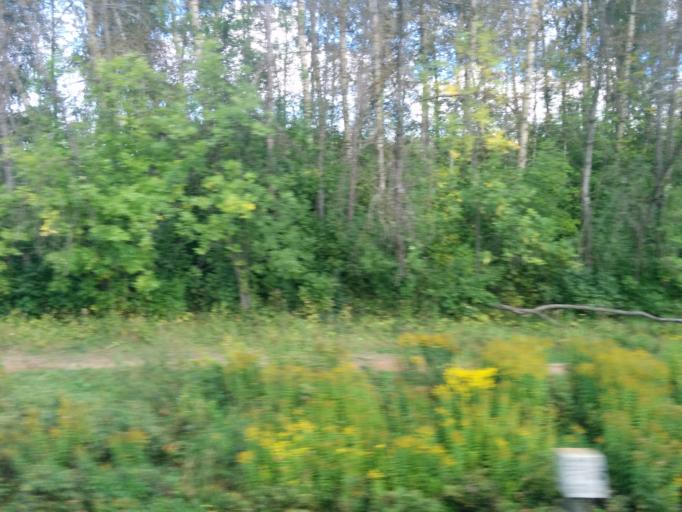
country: RU
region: Moskovskaya
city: Dolgoprudnyy
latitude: 55.9459
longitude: 37.5171
